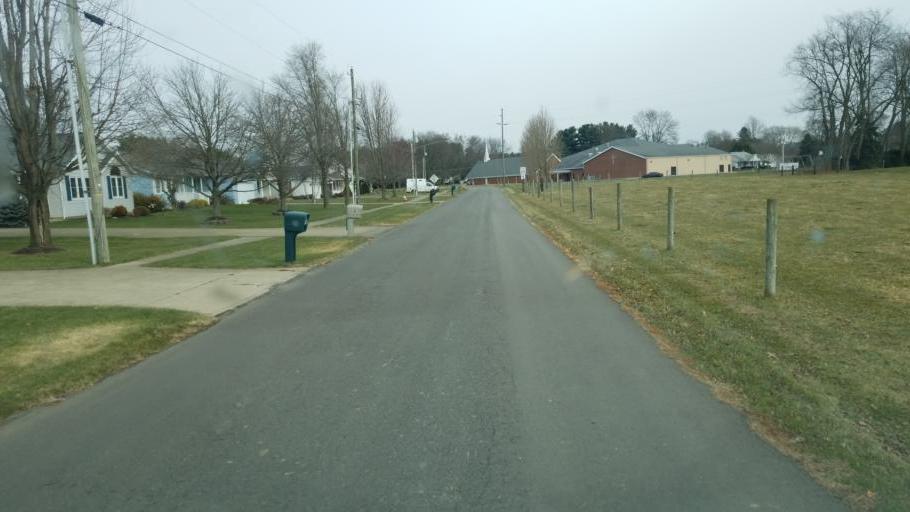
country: US
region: Ohio
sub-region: Sandusky County
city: Bellville
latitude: 40.6146
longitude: -82.5209
